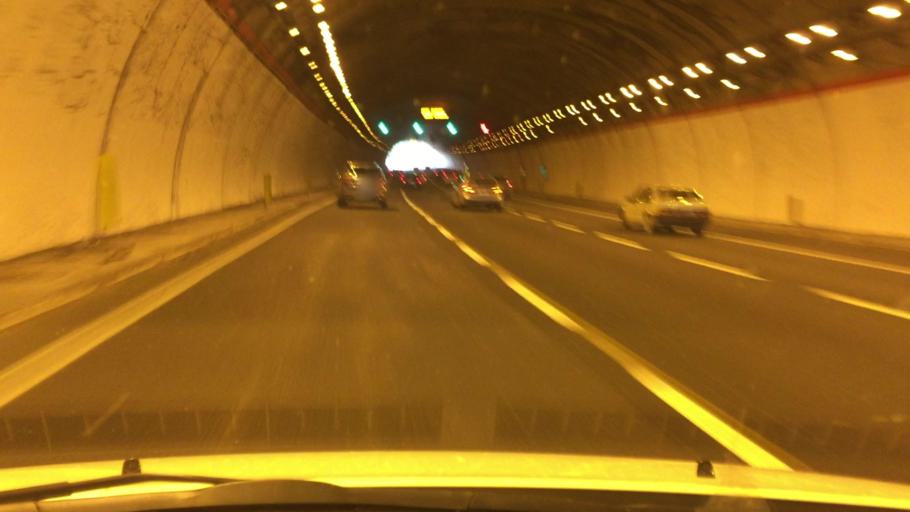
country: VA
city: Vatican City
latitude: 41.9704
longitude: 12.4088
